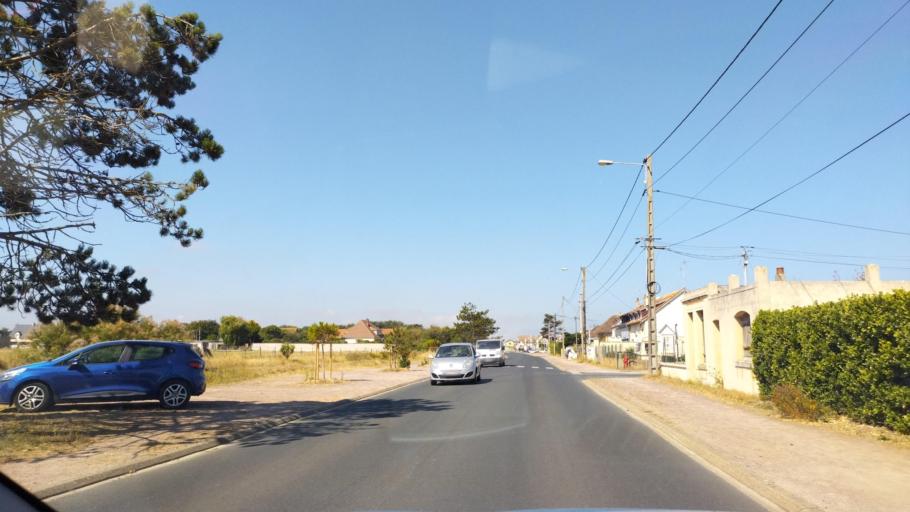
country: FR
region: Lower Normandy
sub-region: Departement du Calvados
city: Bernieres-sur-Mer
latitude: 49.3346
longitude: -0.4137
